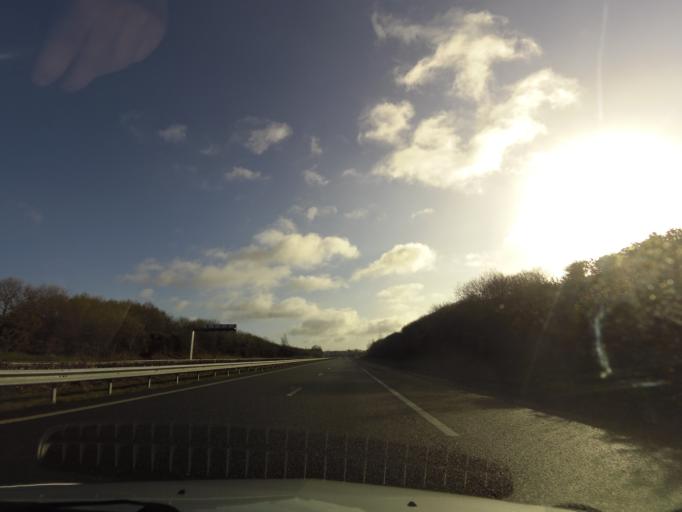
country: FR
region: Brittany
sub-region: Departement d'Ille-et-Vilaine
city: Saint-Sauveur-des-Landes
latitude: 48.3178
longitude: -1.3278
